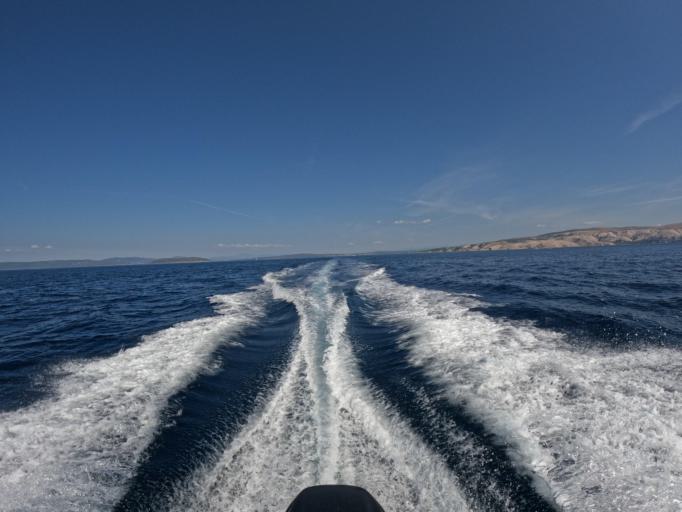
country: HR
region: Primorsko-Goranska
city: Punat
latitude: 44.9125
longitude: 14.6268
